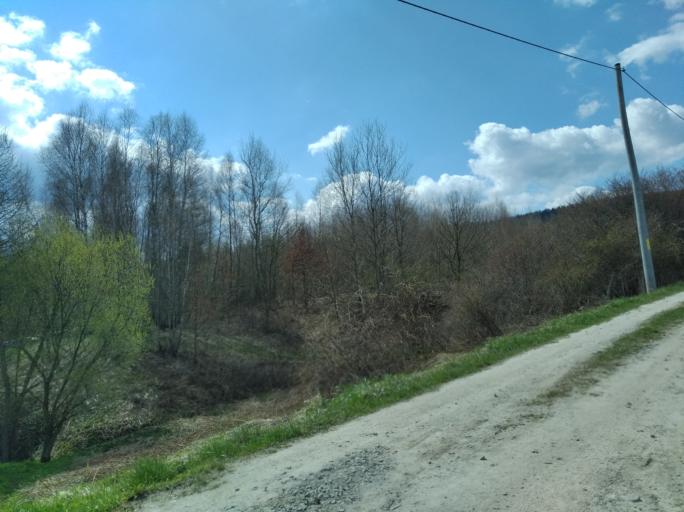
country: PL
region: Subcarpathian Voivodeship
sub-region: Powiat strzyzowski
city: Strzyzow
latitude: 49.8391
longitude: 21.7812
